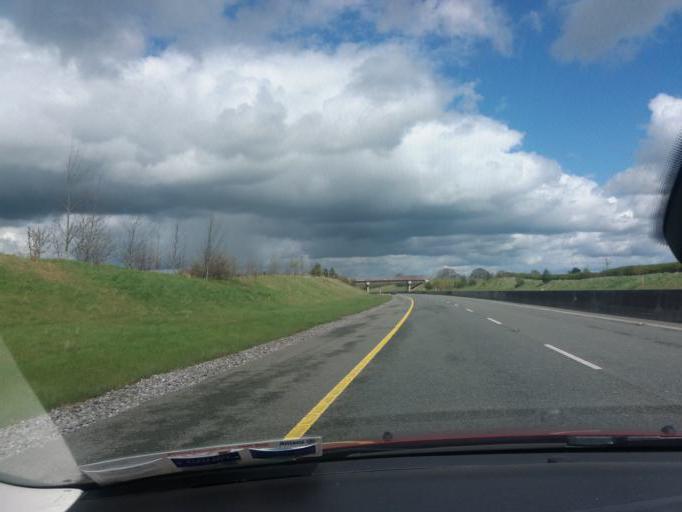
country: IE
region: Leinster
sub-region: Laois
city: Rathdowney
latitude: 52.8114
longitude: -7.4940
